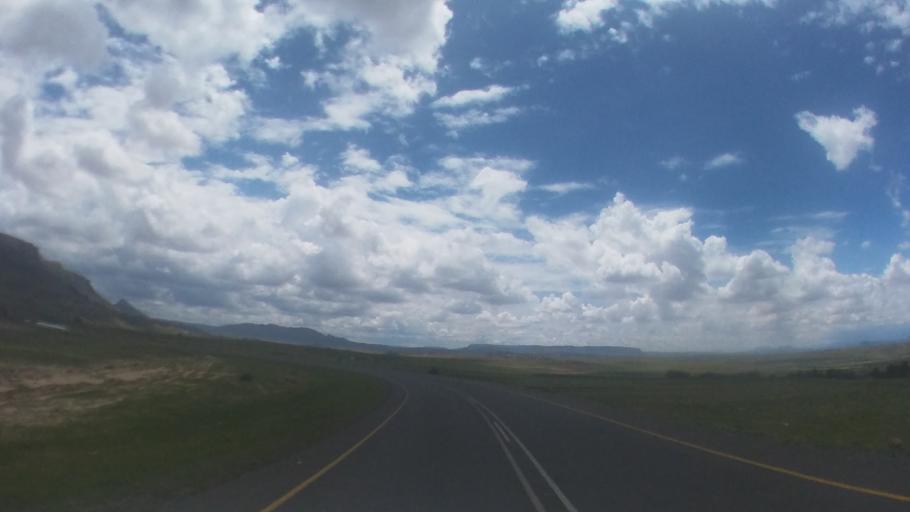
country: LS
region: Maseru
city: Maseru
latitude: -29.4491
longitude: 27.4777
